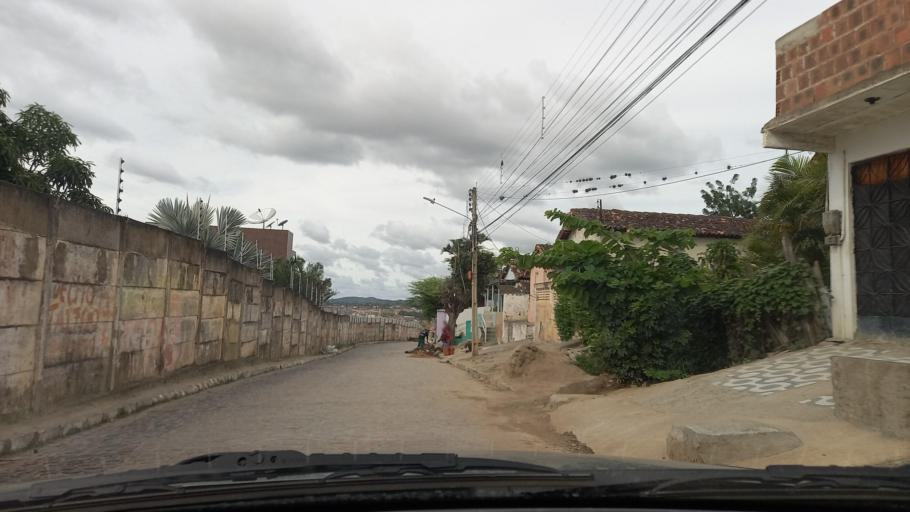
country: BR
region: Pernambuco
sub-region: Gravata
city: Gravata
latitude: -8.2093
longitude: -35.5750
